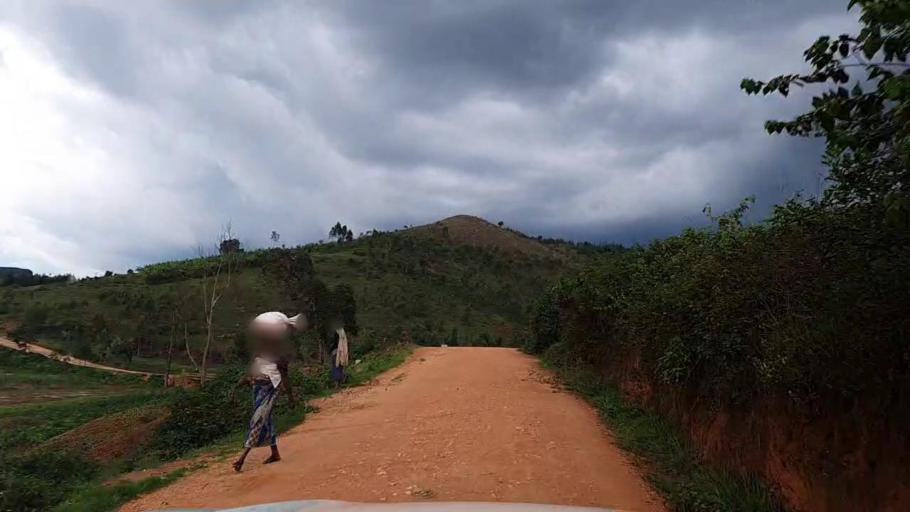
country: RW
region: Southern Province
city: Nyanza
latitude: -2.3926
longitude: 29.6909
